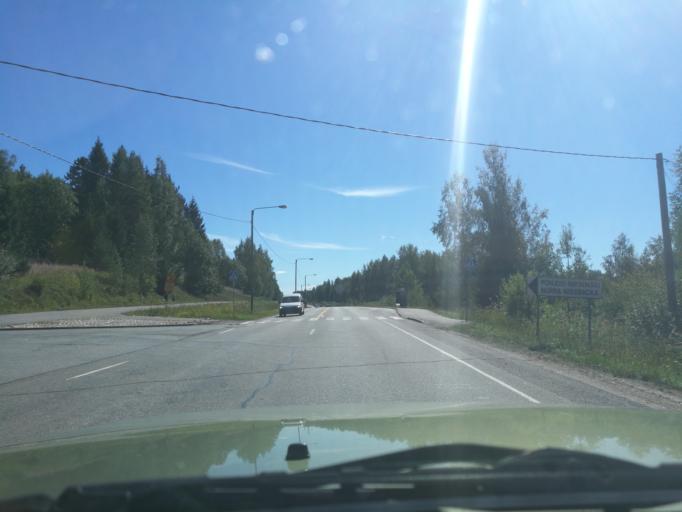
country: FI
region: Uusimaa
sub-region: Helsinki
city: Kerava
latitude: 60.3567
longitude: 25.1272
